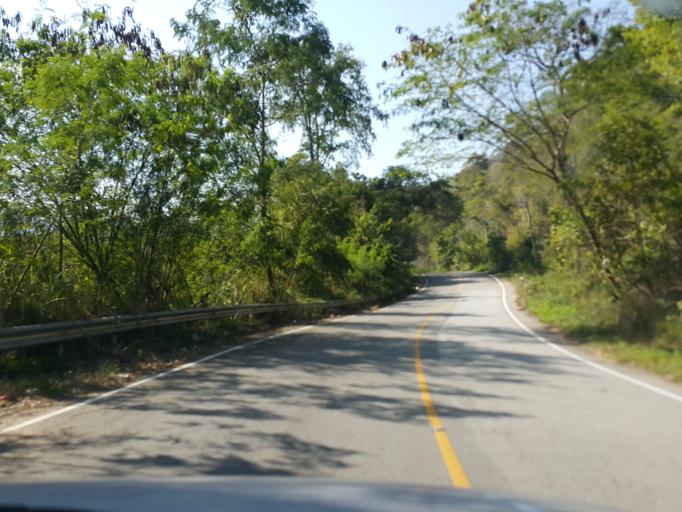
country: TH
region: Chiang Mai
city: Mae Wang
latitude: 18.6180
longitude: 98.7443
